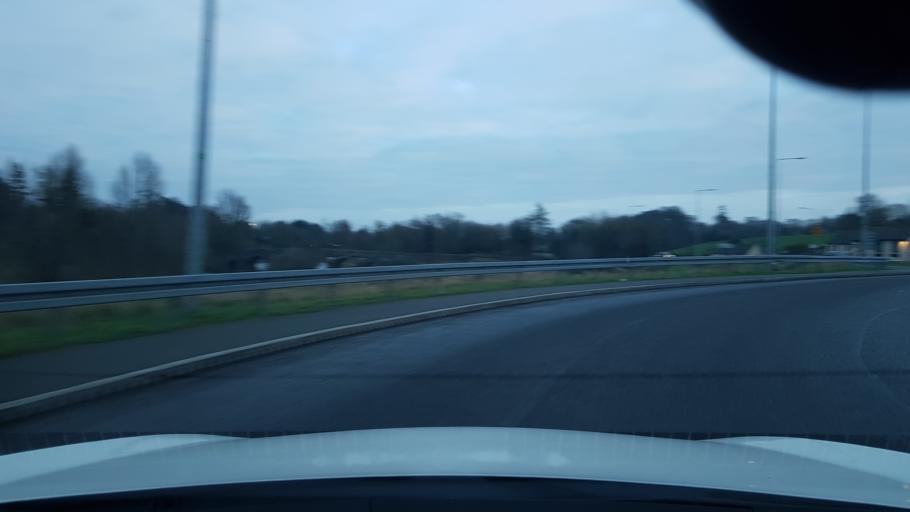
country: IE
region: Leinster
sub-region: An Mhi
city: Navan
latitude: 53.6341
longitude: -6.6647
